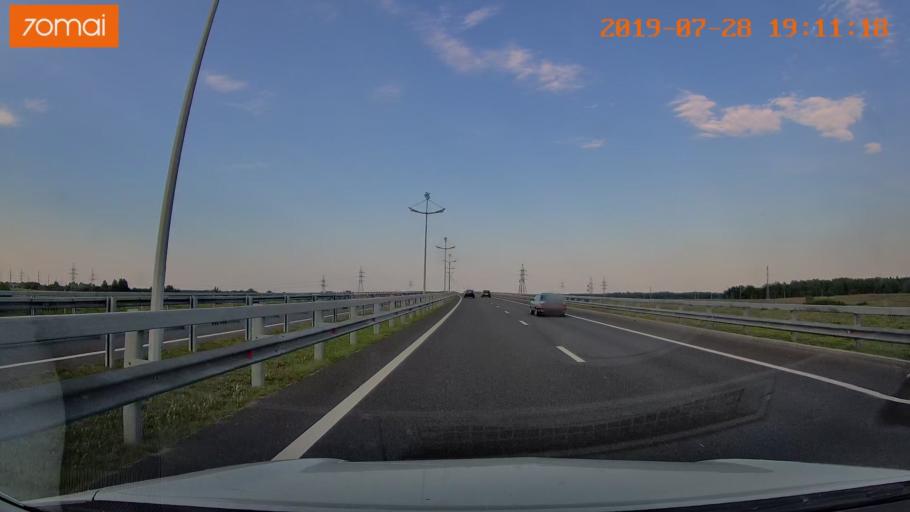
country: RU
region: Kaliningrad
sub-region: Gorod Kaliningrad
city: Pionerskiy
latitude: 54.9128
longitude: 20.2266
